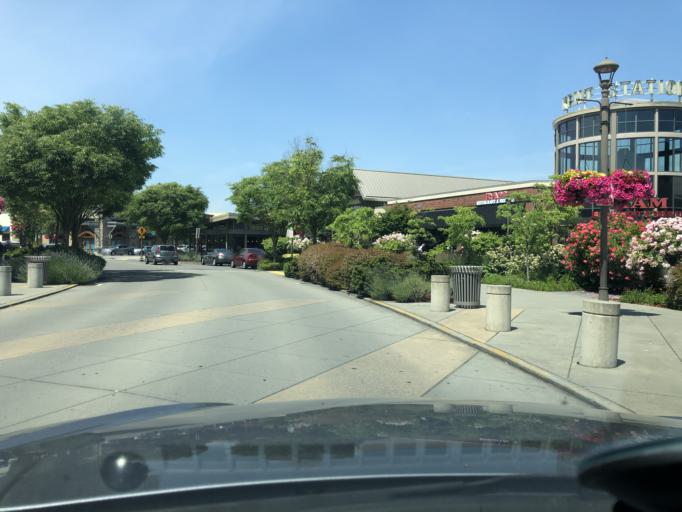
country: US
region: Washington
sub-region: King County
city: Kent
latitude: 47.3847
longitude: -122.2349
